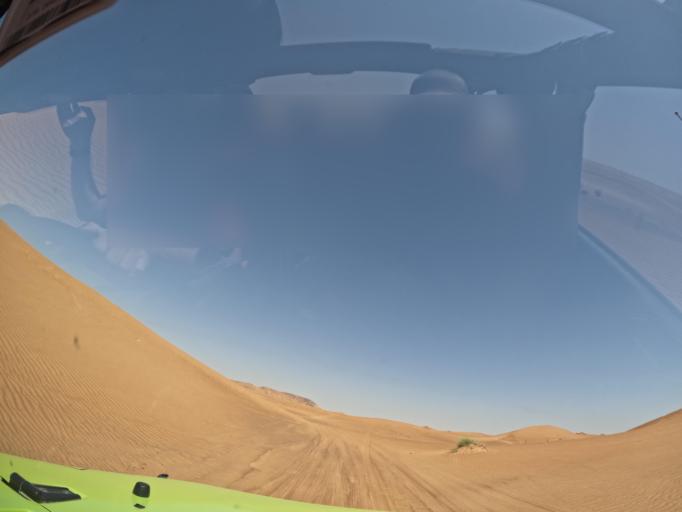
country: AE
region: Ash Shariqah
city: Adh Dhayd
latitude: 25.0047
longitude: 55.7330
